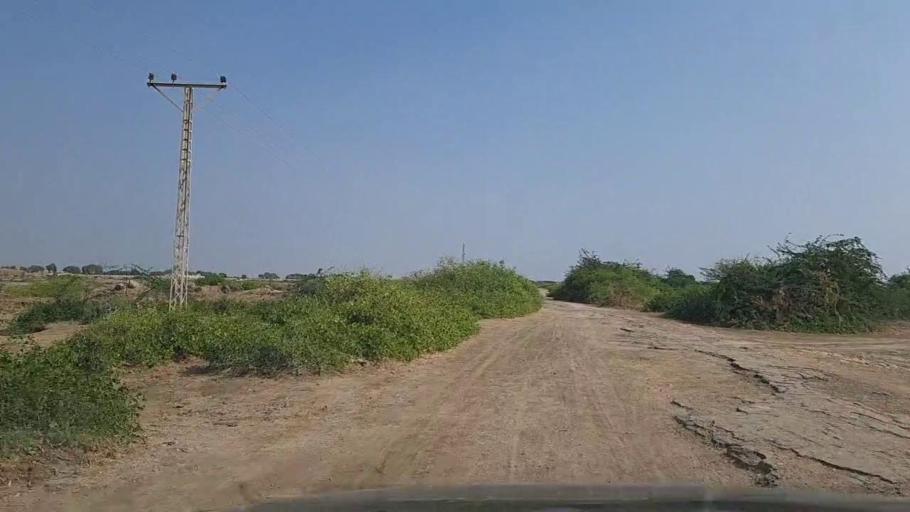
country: PK
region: Sindh
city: Gharo
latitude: 24.7413
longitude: 67.6559
